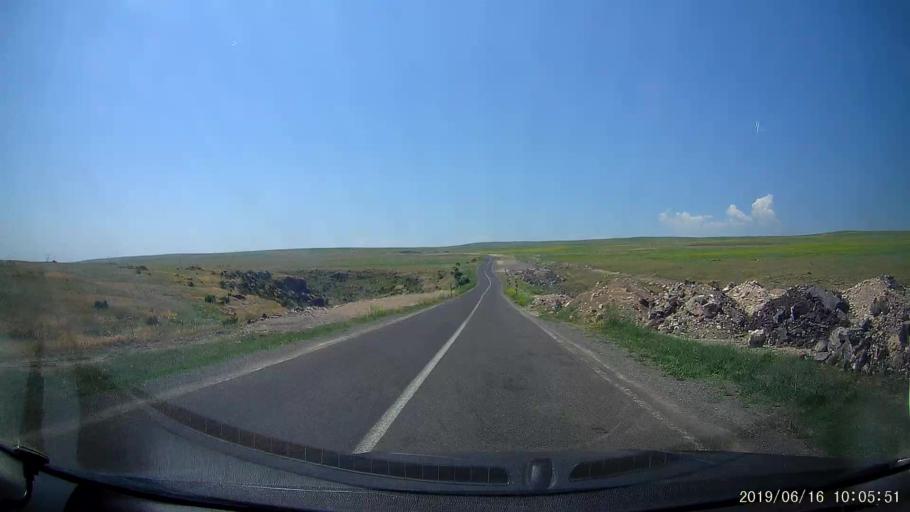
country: TR
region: Kars
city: Digor
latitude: 40.2646
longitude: 43.5399
